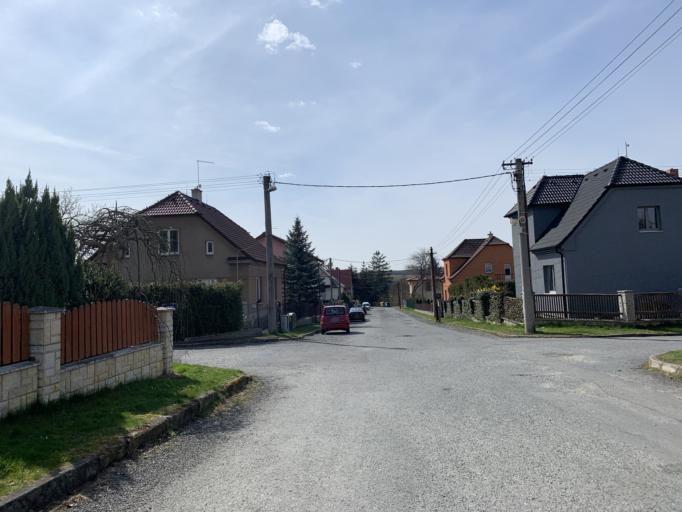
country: CZ
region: Plzensky
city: Stenovice
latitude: 49.6692
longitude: 13.3969
